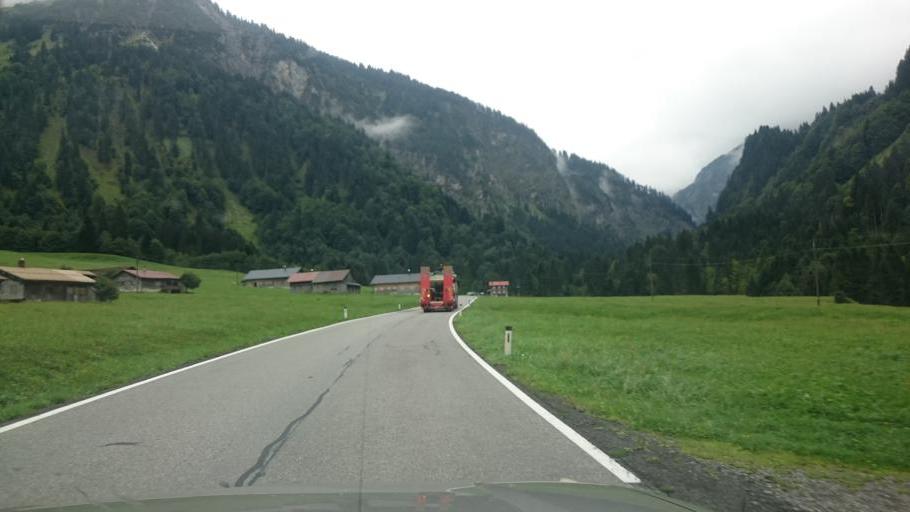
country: AT
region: Vorarlberg
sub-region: Politischer Bezirk Bregenz
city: Schroecken
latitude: 47.2836
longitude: 10.0550
